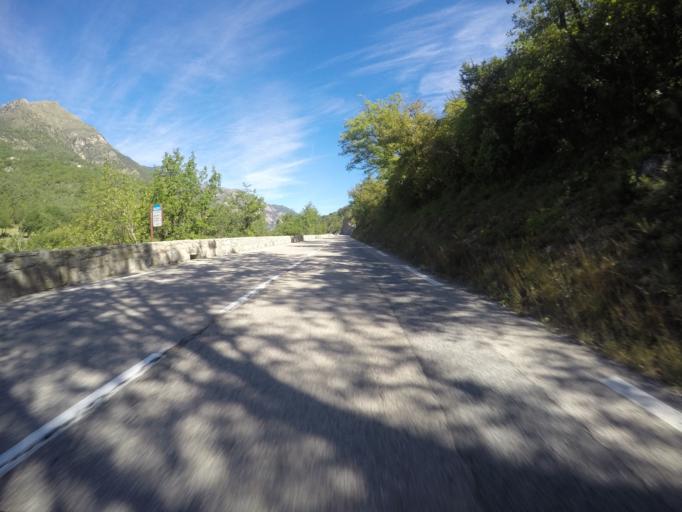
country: FR
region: Provence-Alpes-Cote d'Azur
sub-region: Departement des Alpes-Maritimes
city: Gilette
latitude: 43.9534
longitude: 7.1592
